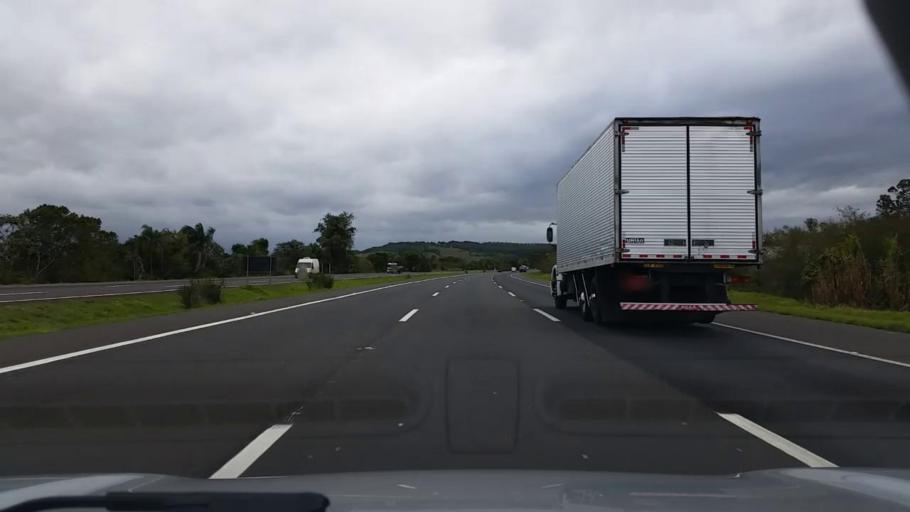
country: BR
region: Rio Grande do Sul
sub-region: Osorio
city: Osorio
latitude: -29.8889
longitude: -50.4594
